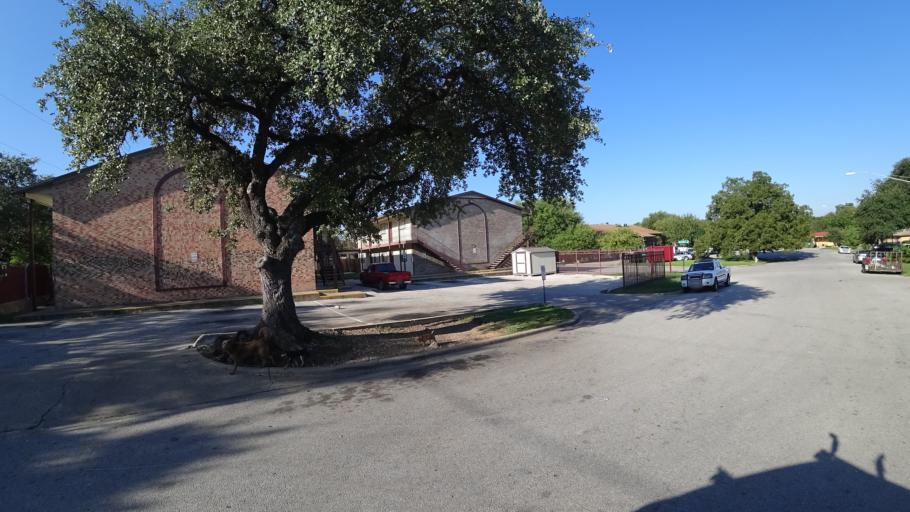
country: US
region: Texas
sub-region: Travis County
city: Austin
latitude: 30.3479
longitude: -97.6986
